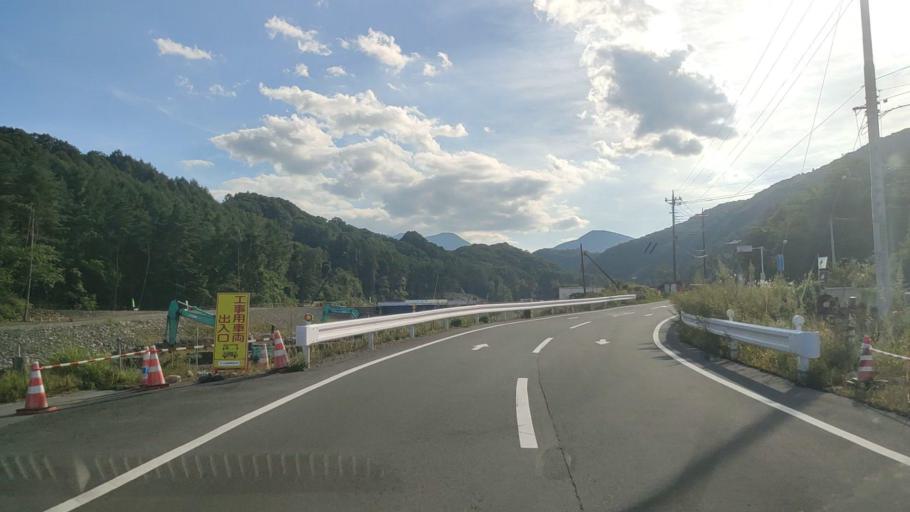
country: JP
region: Nagano
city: Komoro
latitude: 36.4950
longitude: 138.4947
